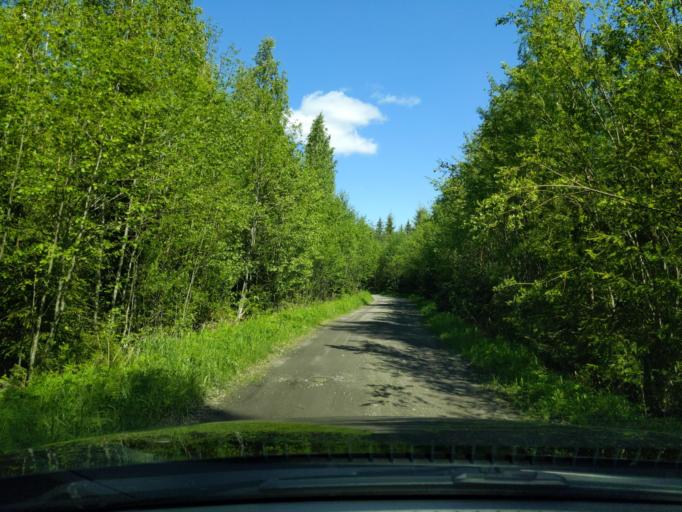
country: FI
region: Paijanne Tavastia
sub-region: Lahti
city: Lahti
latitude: 61.0581
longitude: 25.7007
